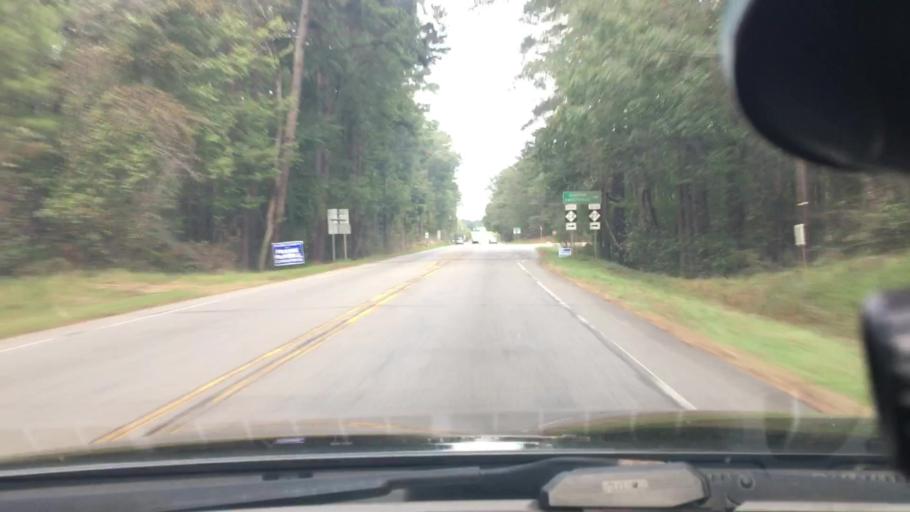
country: US
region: North Carolina
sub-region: Moore County
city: Carthage
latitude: 35.3485
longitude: -79.3672
